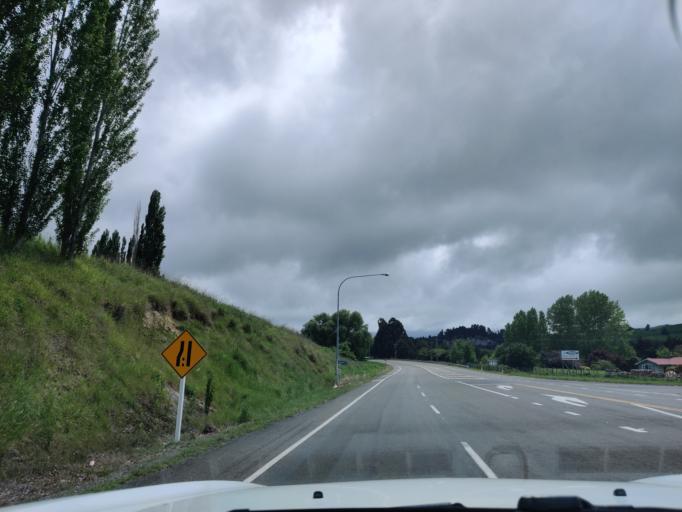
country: NZ
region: Manawatu-Wanganui
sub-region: Ruapehu District
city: Waiouru
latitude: -39.6610
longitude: 175.7813
